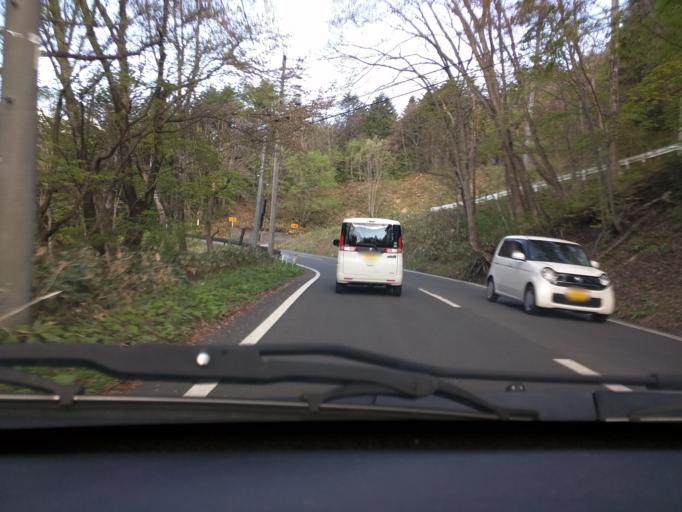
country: JP
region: Nagano
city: Nagano-shi
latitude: 36.7328
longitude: 138.0808
